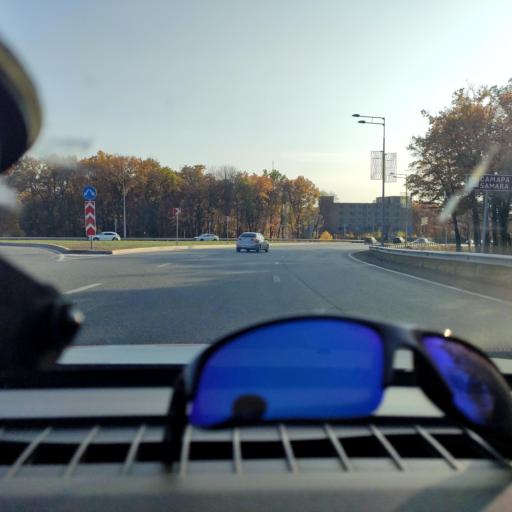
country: RU
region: Samara
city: Petra-Dubrava
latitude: 53.3088
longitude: 50.2343
